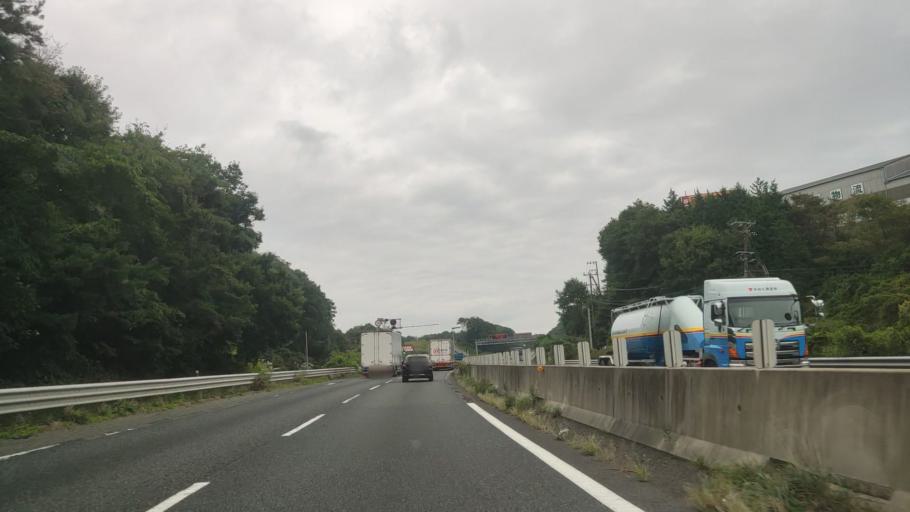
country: JP
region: Mie
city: Nabari
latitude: 34.6293
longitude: 135.9875
